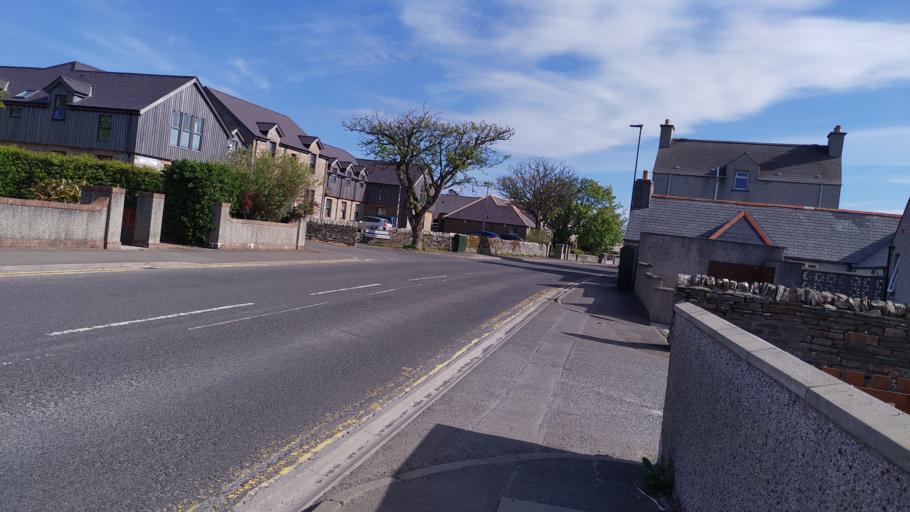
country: GB
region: Scotland
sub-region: Orkney Islands
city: Orkney
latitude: 58.9757
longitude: -2.9696
